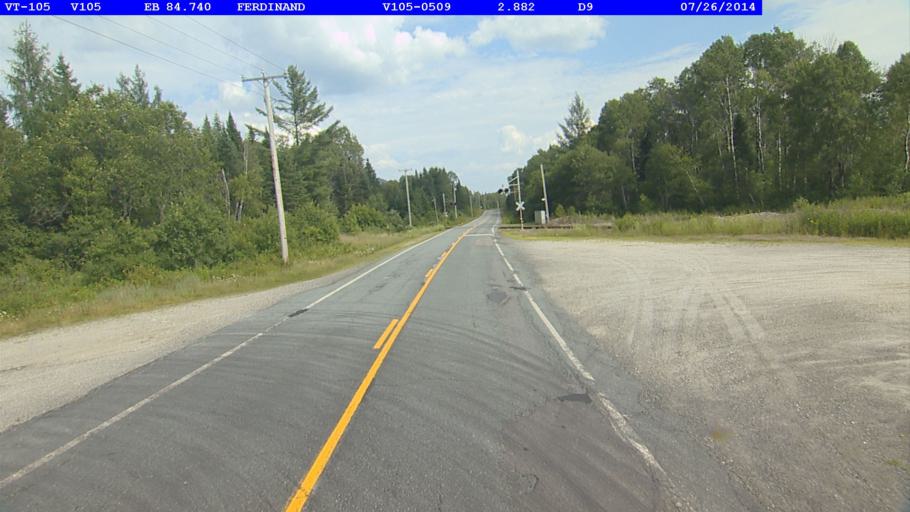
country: US
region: New Hampshire
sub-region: Coos County
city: Stratford
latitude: 44.7761
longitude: -71.7485
